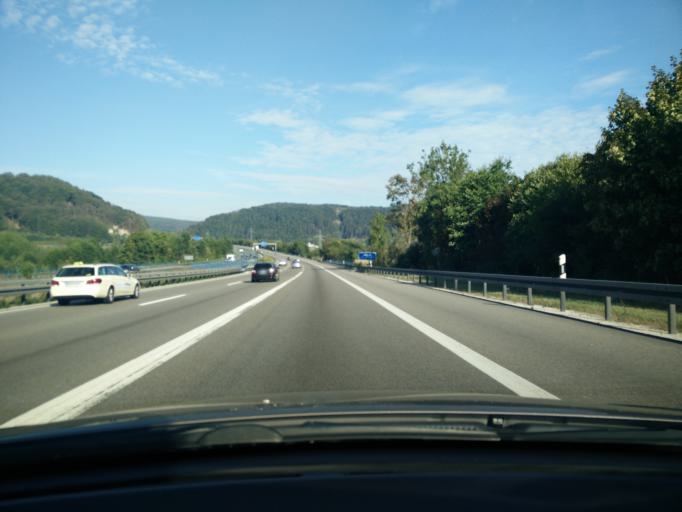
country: DE
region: Bavaria
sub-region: Regierungsbezirk Mittelfranken
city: Greding
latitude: 48.9908
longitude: 11.3843
